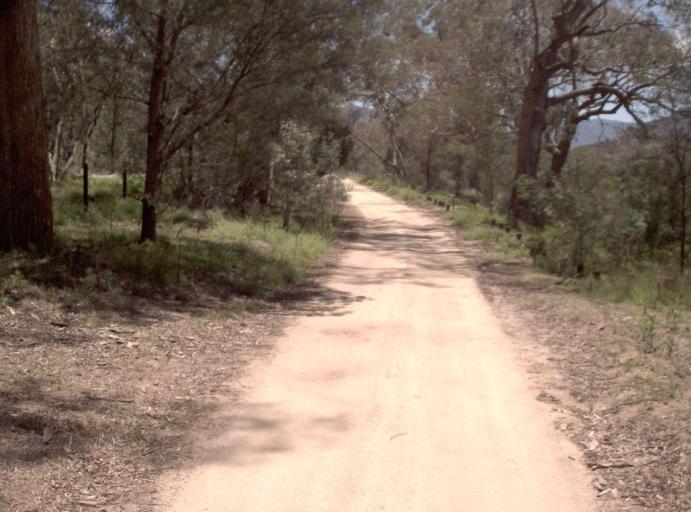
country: AU
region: New South Wales
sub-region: Snowy River
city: Jindabyne
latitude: -36.8880
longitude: 148.4205
